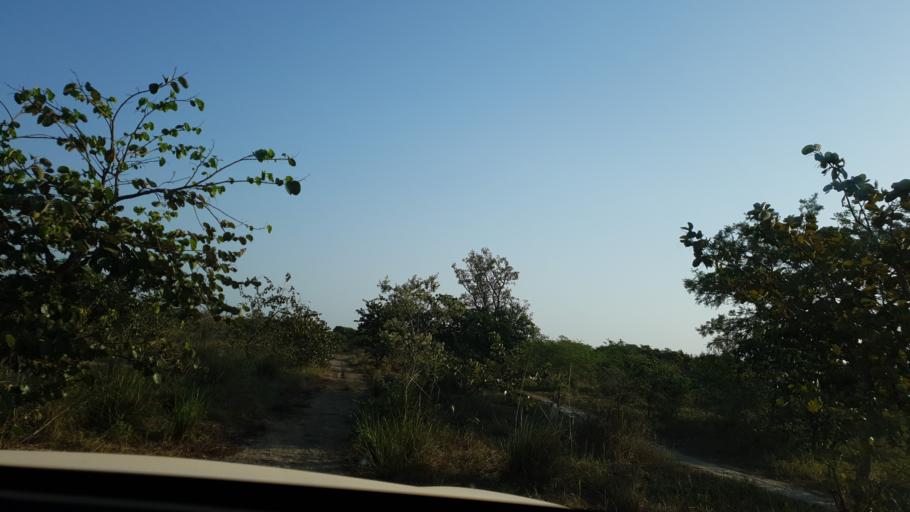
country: ML
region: Sikasso
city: Kadiolo
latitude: 10.6648
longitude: -5.8035
